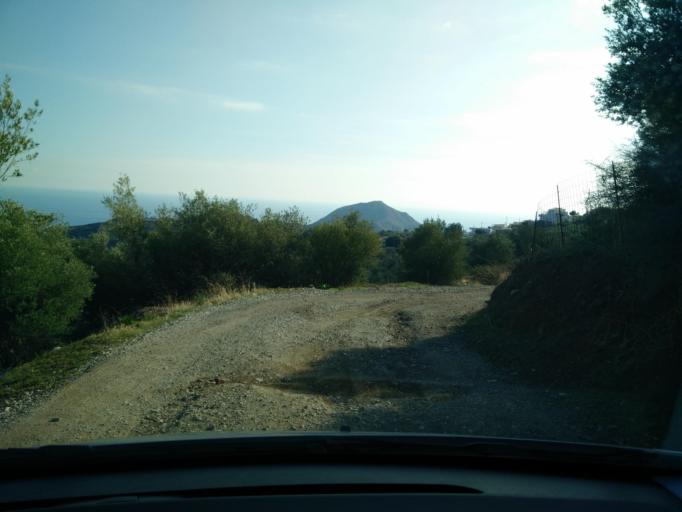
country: GR
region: Crete
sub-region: Nomos Lasithiou
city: Gra Liyia
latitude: 35.0314
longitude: 25.5675
